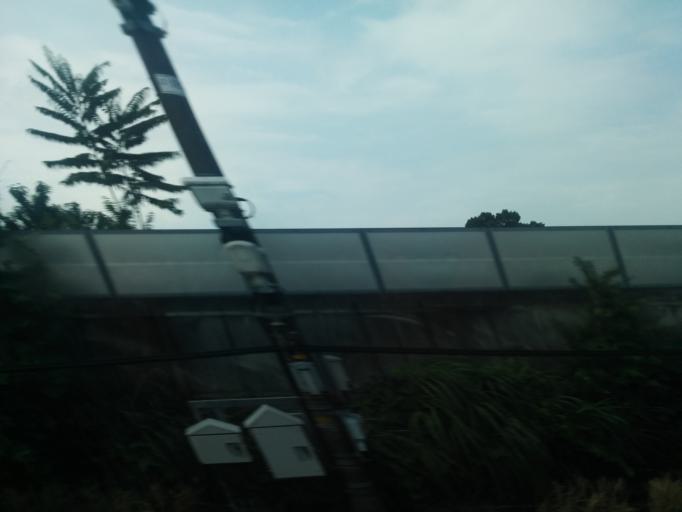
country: JP
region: Shizuoka
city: Fuji
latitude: 35.1512
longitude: 138.7778
